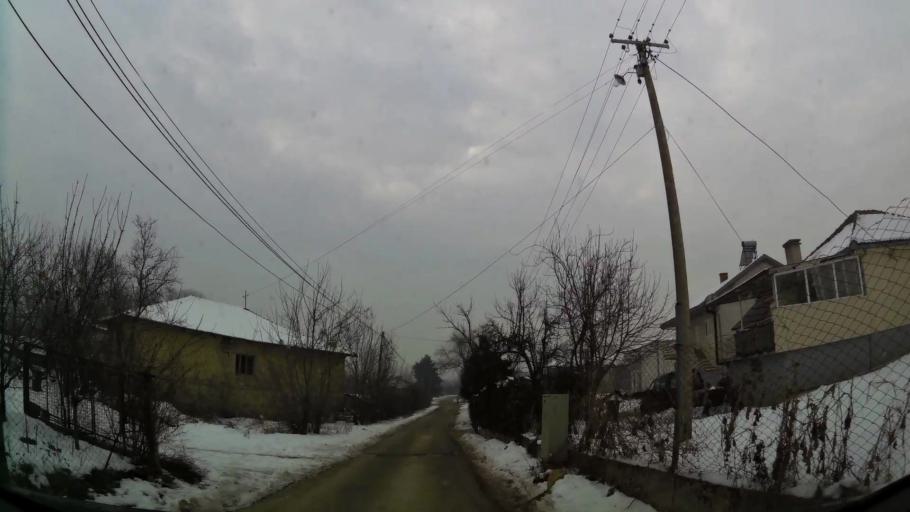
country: MK
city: Kondovo
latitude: 42.0499
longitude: 21.3432
